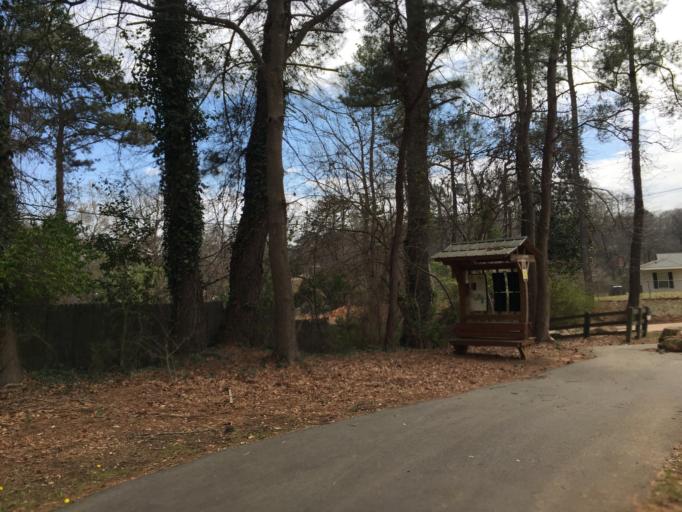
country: US
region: South Carolina
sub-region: Greenville County
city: Mauldin
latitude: 34.7837
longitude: -82.3658
